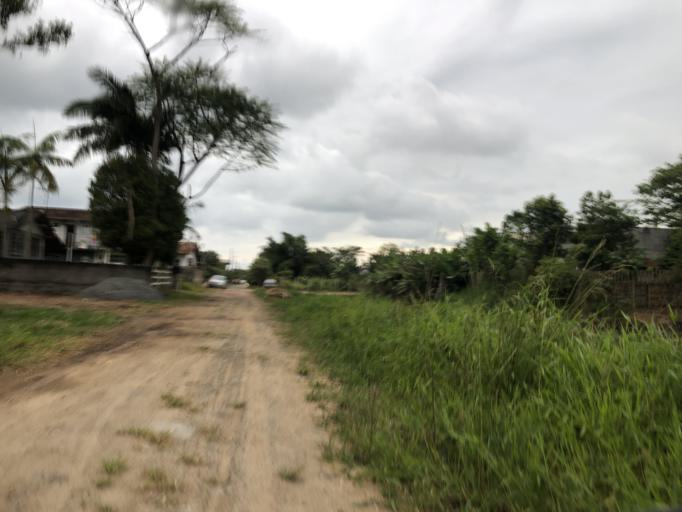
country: BR
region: Santa Catarina
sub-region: Sao Francisco Do Sul
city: Sao Francisco do Sul
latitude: -26.2192
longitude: -48.5315
